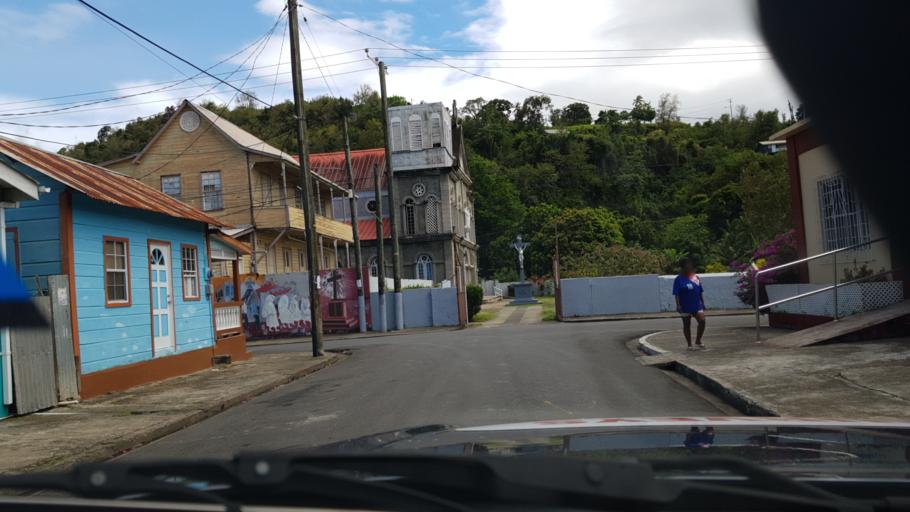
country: LC
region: Anse-la-Raye
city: Anse La Raye
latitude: 13.9399
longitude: -61.0430
